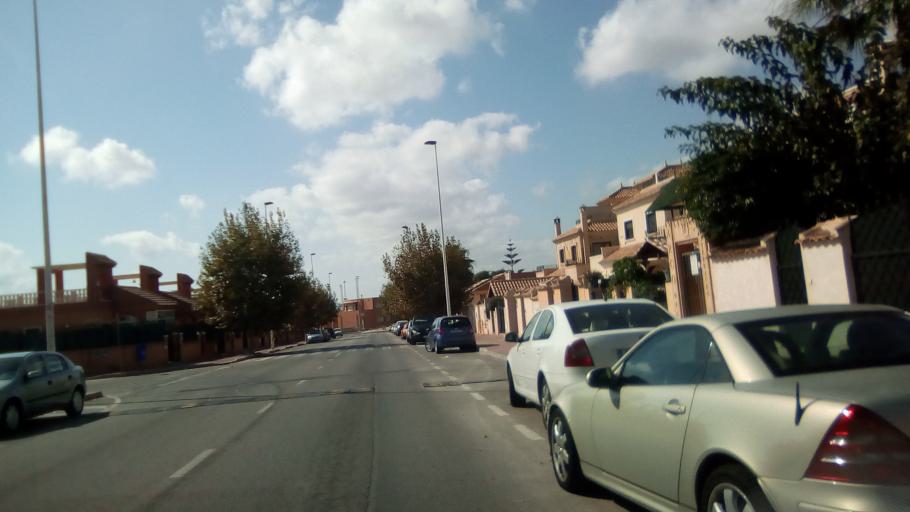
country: ES
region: Valencia
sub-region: Provincia de Alicante
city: Torrevieja
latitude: 38.0003
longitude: -0.6766
